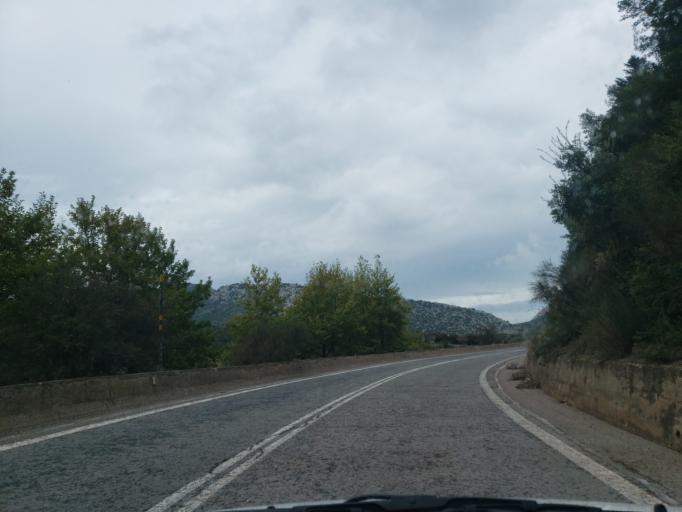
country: GR
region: Central Greece
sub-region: Nomos Fokidos
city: Amfissa
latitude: 38.6429
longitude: 22.4023
